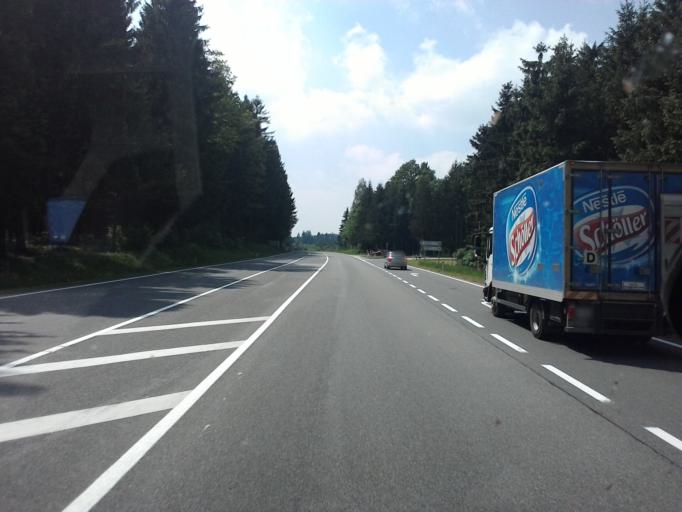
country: AT
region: Upper Austria
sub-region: Politischer Bezirk Steyr-Land
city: Sierning
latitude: 48.0350
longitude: 14.2941
